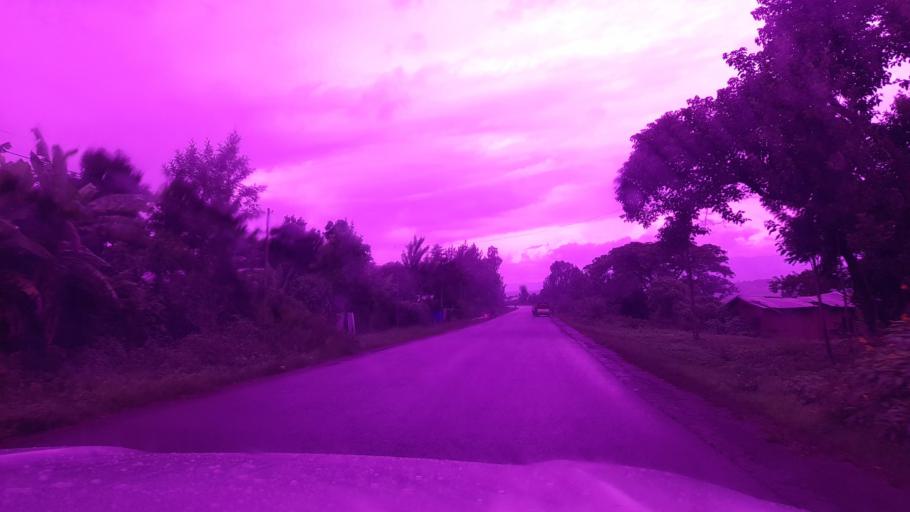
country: ET
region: Oromiya
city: Jima
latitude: 7.7078
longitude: 37.0655
